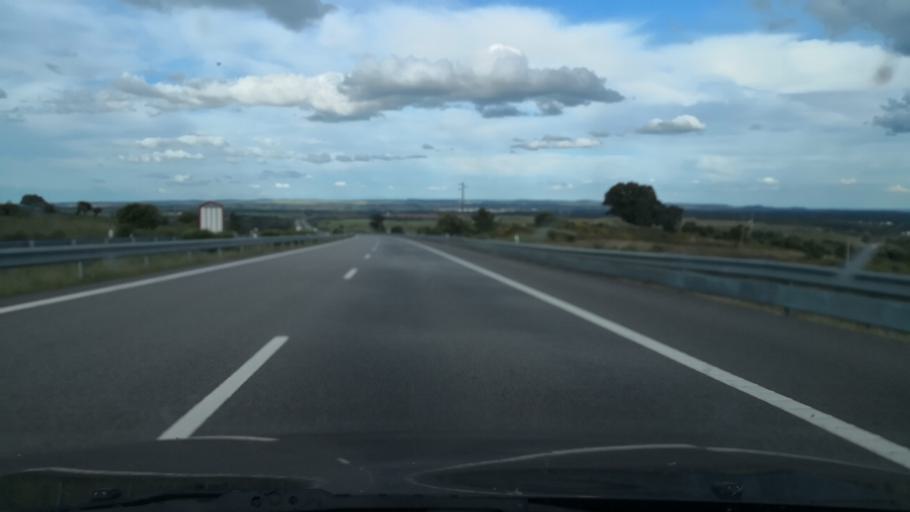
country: PT
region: Evora
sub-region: Borba
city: Borba
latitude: 38.8215
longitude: -7.4470
